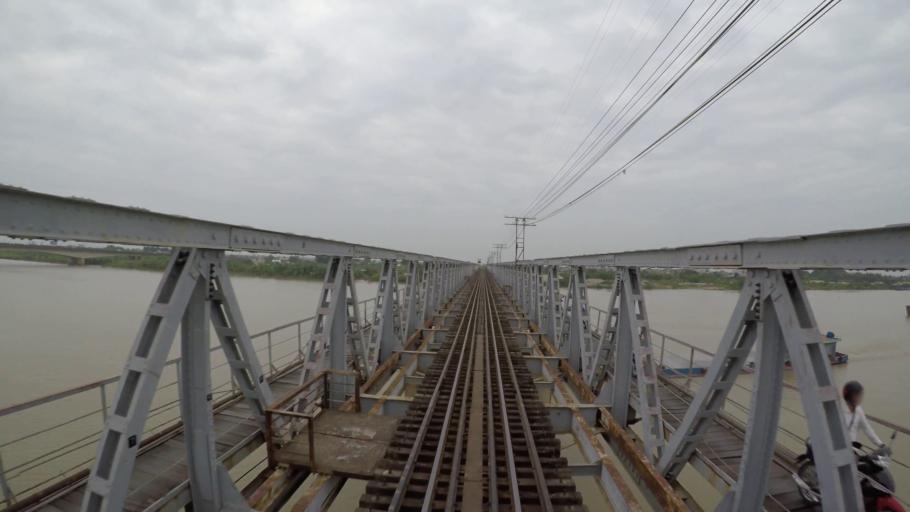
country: VN
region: Hai Duong
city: Thanh Pho Hai Duong
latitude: 20.9552
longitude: 106.3640
